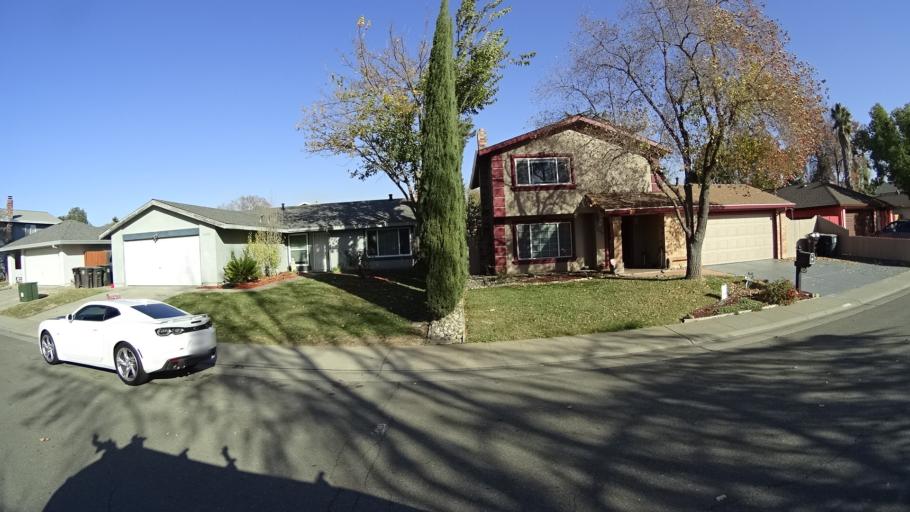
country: US
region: California
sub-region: Sacramento County
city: Antelope
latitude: 38.6982
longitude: -121.3135
